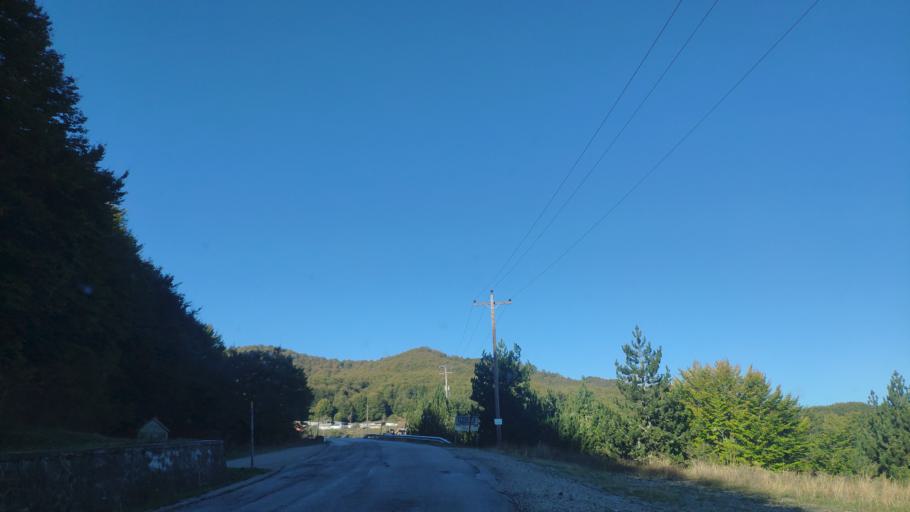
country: GR
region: Epirus
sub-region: Nomos Ioanninon
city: Metsovo
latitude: 39.7795
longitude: 21.1663
